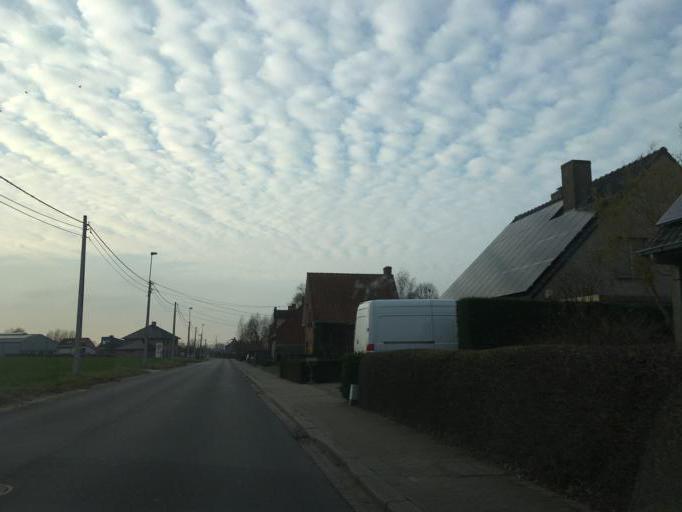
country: BE
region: Flanders
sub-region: Provincie West-Vlaanderen
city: Roeselare
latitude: 50.9289
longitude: 3.1141
